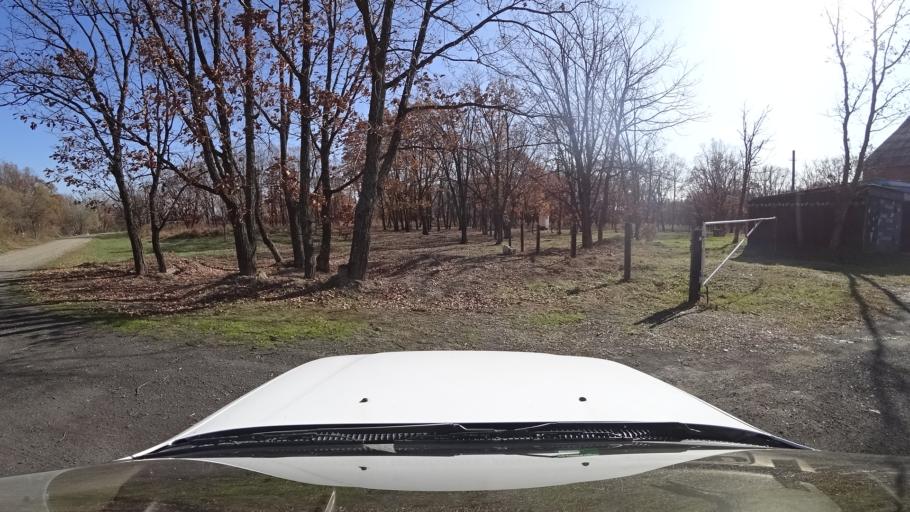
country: RU
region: Primorskiy
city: Dal'nerechensk
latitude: 45.8828
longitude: 133.7229
